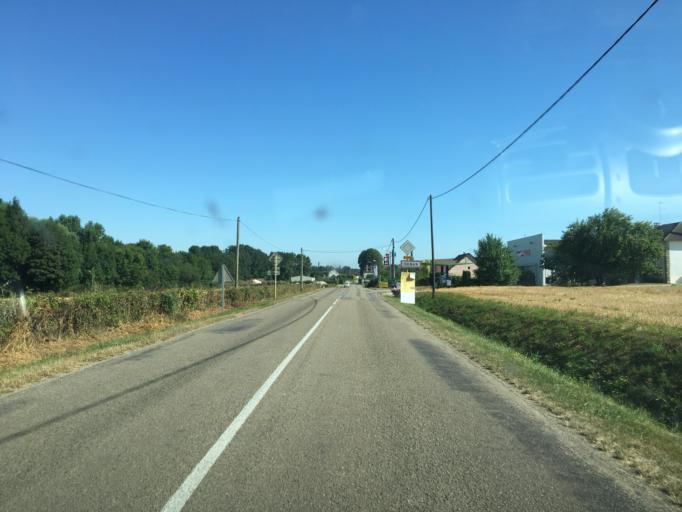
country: FR
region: Bourgogne
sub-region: Departement de l'Yonne
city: Aillant-sur-Tholon
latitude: 47.9063
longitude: 3.3574
